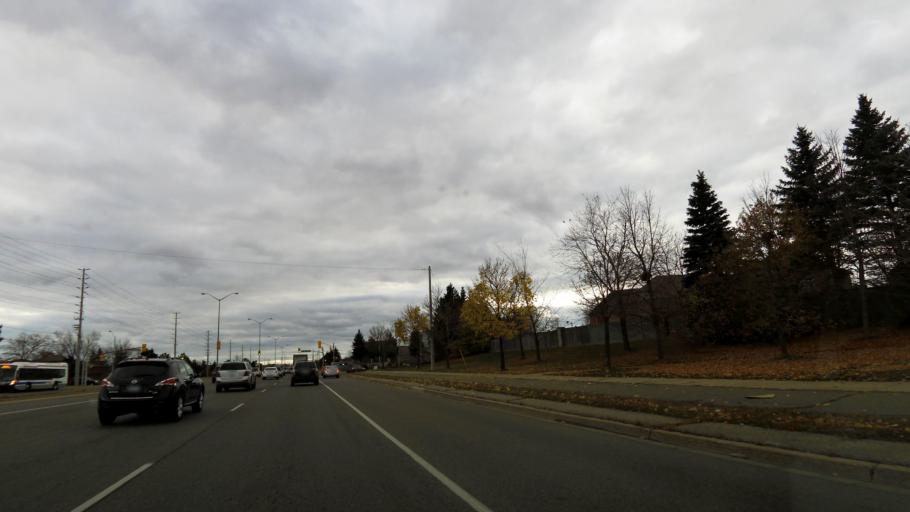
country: CA
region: Ontario
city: Brampton
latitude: 43.7390
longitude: -79.7503
